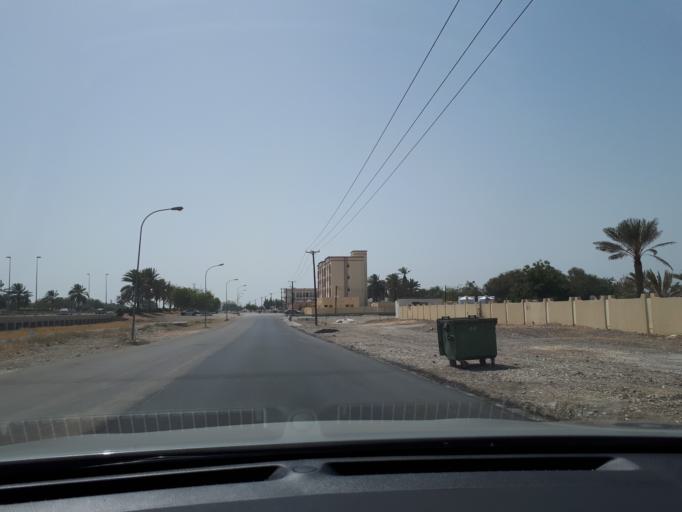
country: OM
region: Muhafazat Masqat
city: As Sib al Jadidah
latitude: 23.6936
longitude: 58.0687
